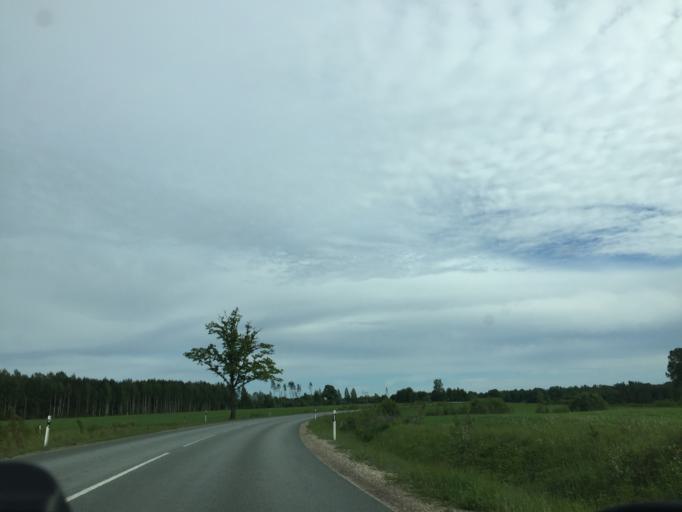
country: LV
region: Beverina
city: Murmuiza
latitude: 57.4655
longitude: 25.4144
